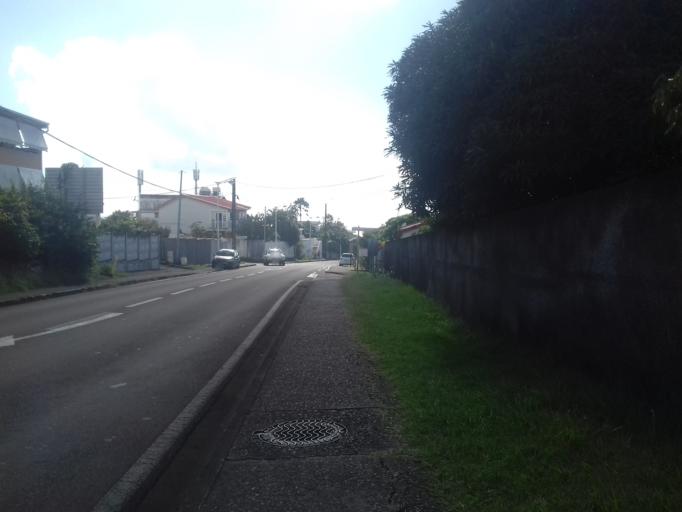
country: MQ
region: Martinique
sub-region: Martinique
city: Fort-de-France
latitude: 14.6180
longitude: -61.0965
